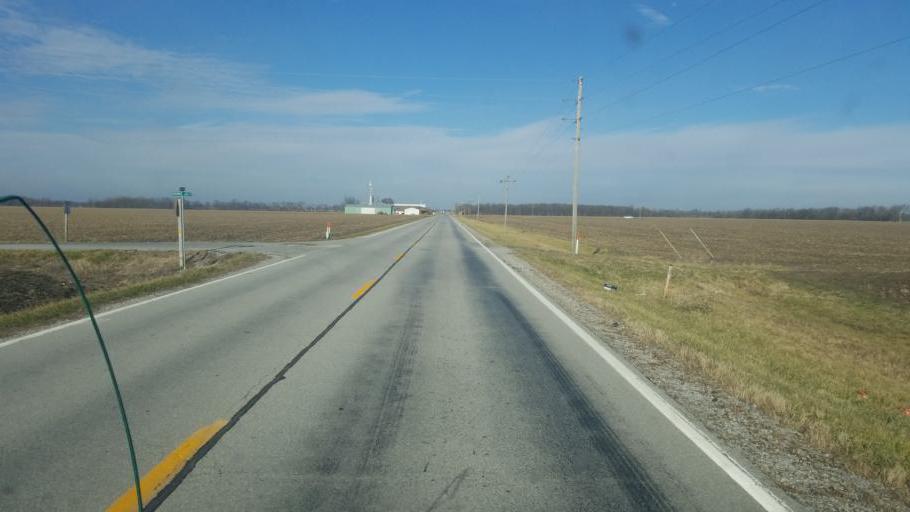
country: US
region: Illinois
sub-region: Saline County
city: Eldorado
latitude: 37.8667
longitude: -88.4529
